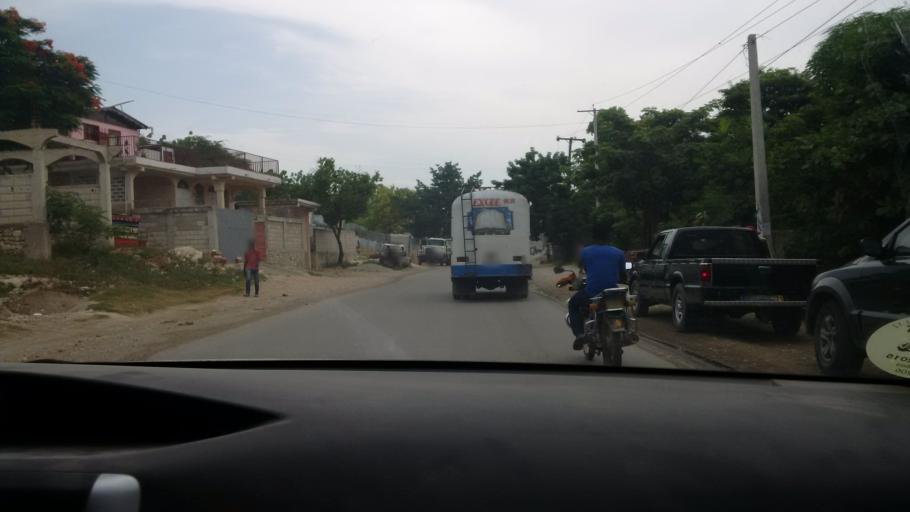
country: HT
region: Ouest
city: Gressier
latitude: 18.5434
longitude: -72.5198
